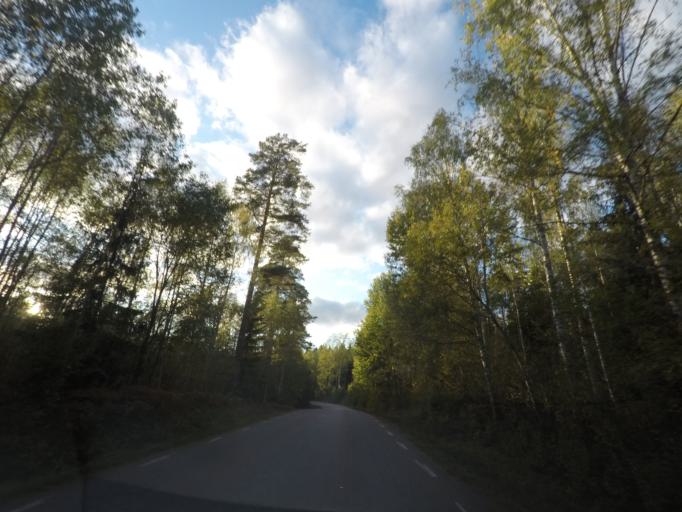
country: SE
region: Vaestmanland
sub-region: Kungsors Kommun
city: Kungsoer
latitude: 59.5088
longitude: 16.0892
